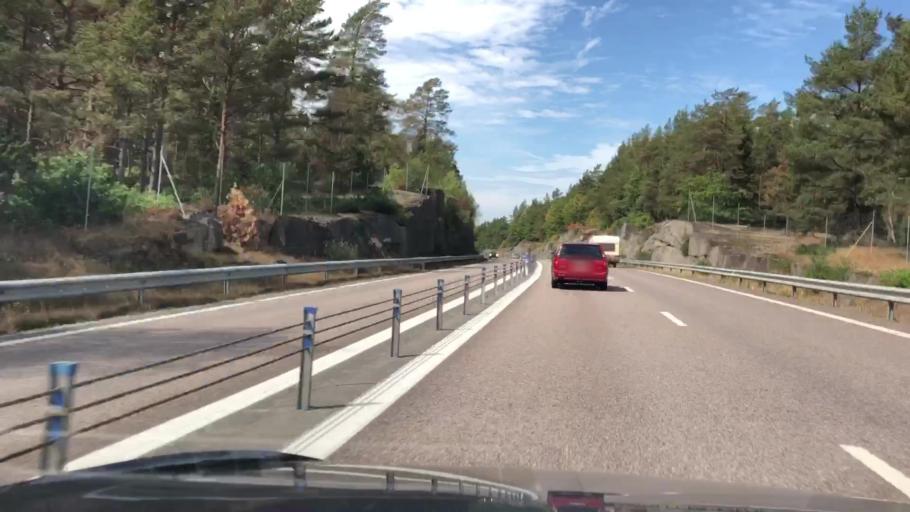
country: SE
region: Blekinge
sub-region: Ronneby Kommun
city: Kallinge
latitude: 56.2128
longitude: 15.3161
